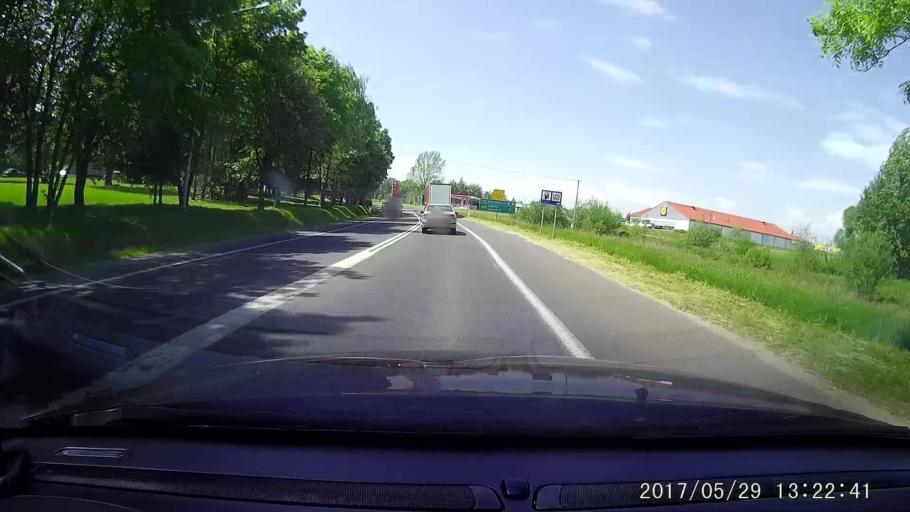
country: PL
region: Lower Silesian Voivodeship
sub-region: Powiat lwowecki
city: Gryfow Slaski
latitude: 51.0348
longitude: 15.4188
